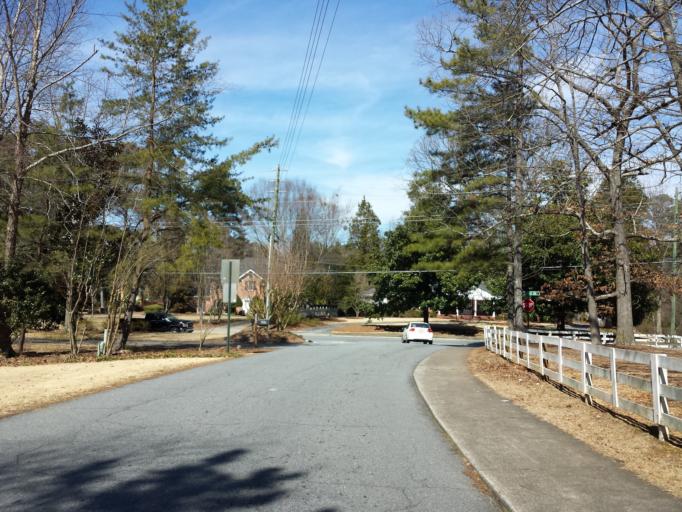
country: US
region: Georgia
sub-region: Cobb County
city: Smyrna
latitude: 33.9416
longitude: -84.4719
